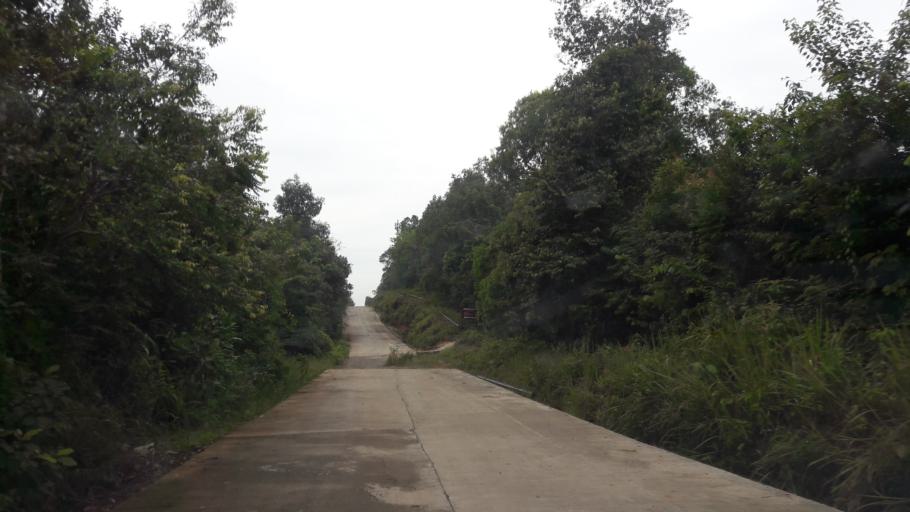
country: ID
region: South Sumatra
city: Gunungmenang
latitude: -3.1965
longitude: 103.8498
